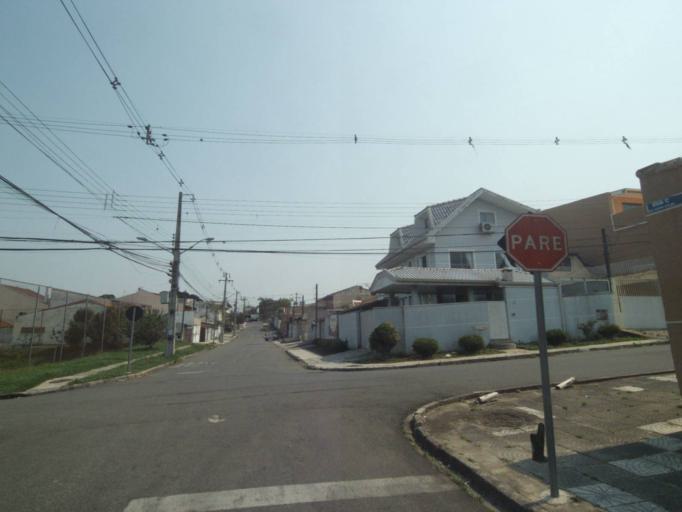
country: BR
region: Parana
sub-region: Sao Jose Dos Pinhais
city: Sao Jose dos Pinhais
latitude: -25.5249
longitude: -49.2430
